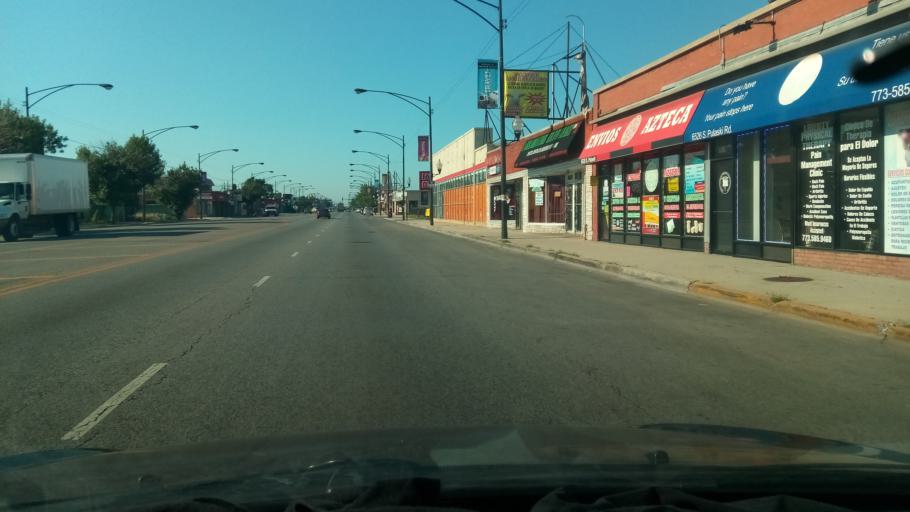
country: US
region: Illinois
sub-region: Cook County
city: Hometown
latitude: 41.7752
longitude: -87.7228
